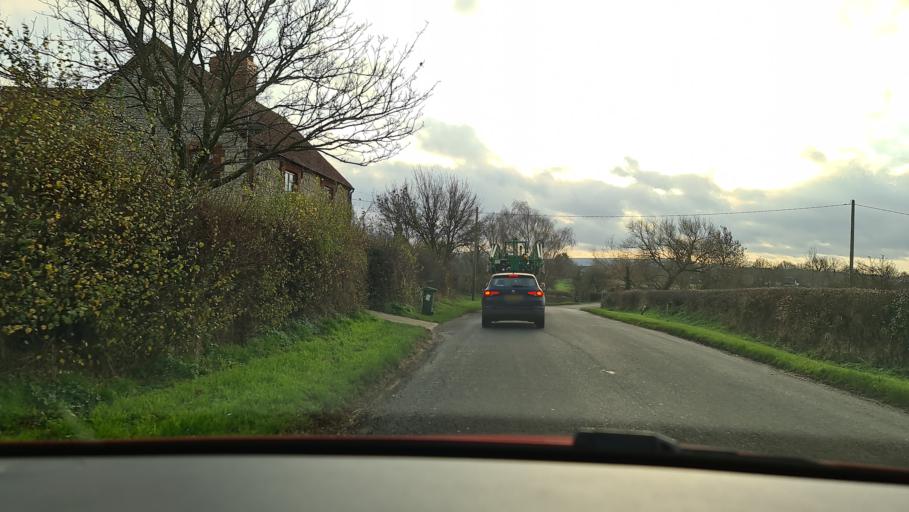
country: GB
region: England
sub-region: Buckinghamshire
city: Stone
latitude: 51.7805
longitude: -0.8779
